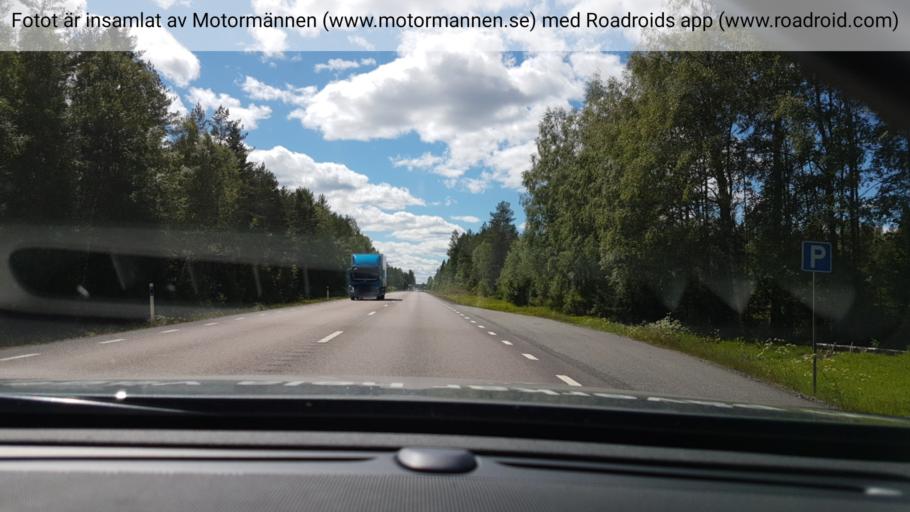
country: SE
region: Vaesterbotten
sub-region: Skelleftea Kommun
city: Burea
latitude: 64.3140
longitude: 21.1594
